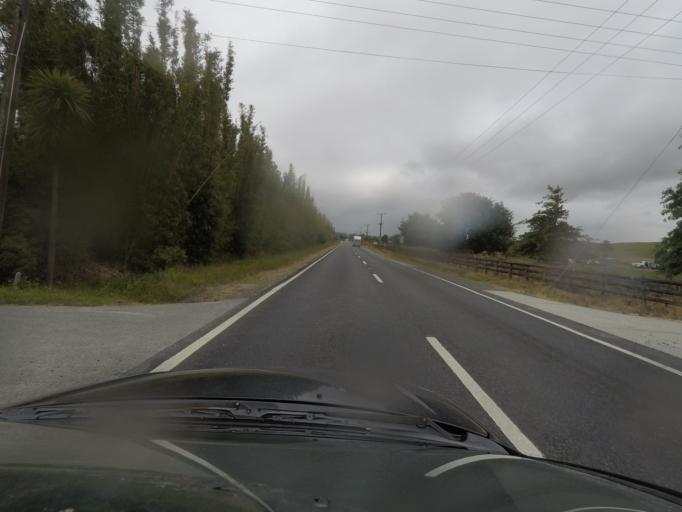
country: NZ
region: Auckland
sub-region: Auckland
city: Warkworth
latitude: -36.3451
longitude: 174.7087
